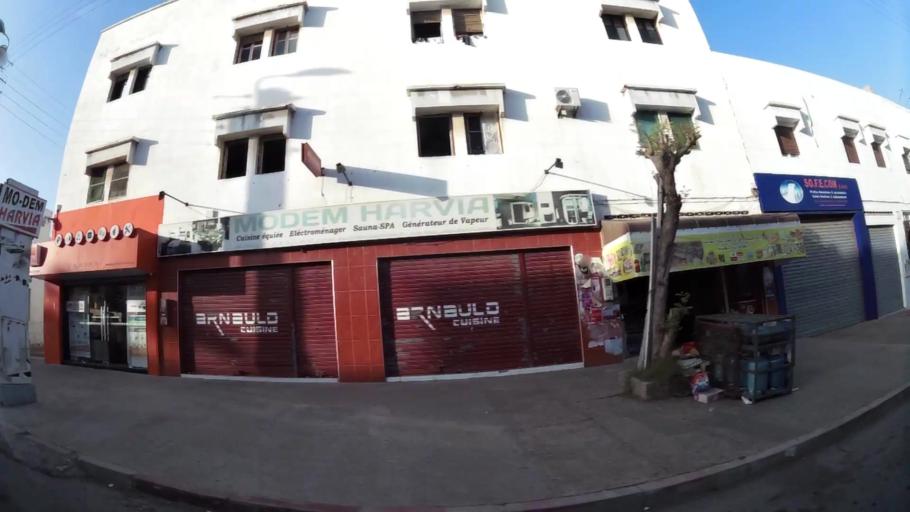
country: MA
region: Oued ed Dahab-Lagouira
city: Dakhla
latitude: 30.4126
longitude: -9.5478
